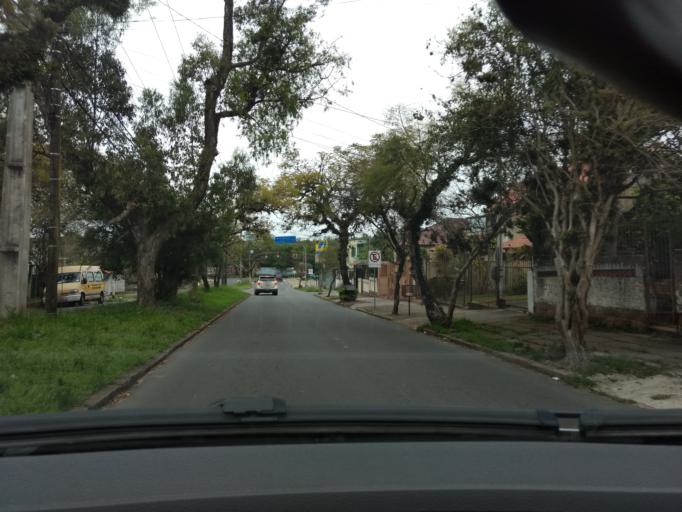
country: BR
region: Rio Grande do Sul
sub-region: Cachoeirinha
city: Cachoeirinha
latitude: -30.0313
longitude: -51.1364
